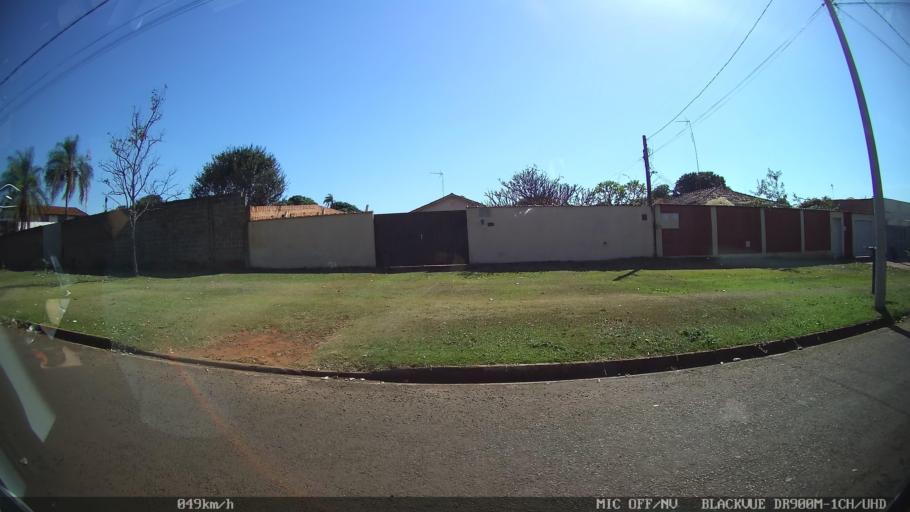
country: BR
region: Sao Paulo
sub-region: Batatais
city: Batatais
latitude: -20.8849
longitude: -47.5681
